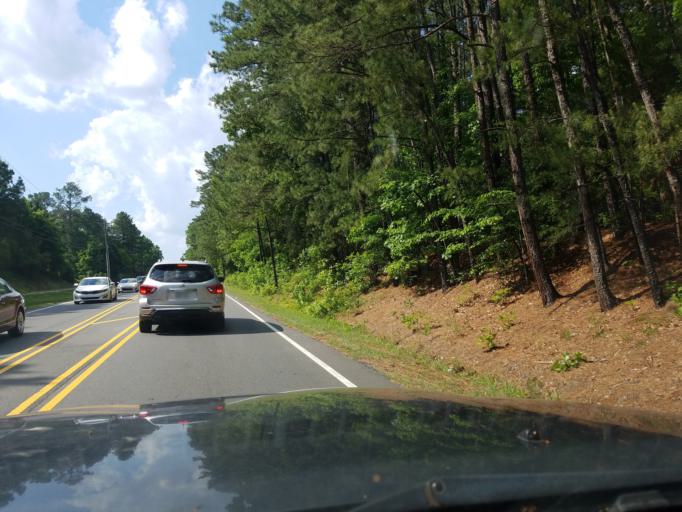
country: US
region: North Carolina
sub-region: Durham County
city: Durham
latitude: 35.9407
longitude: -78.9652
